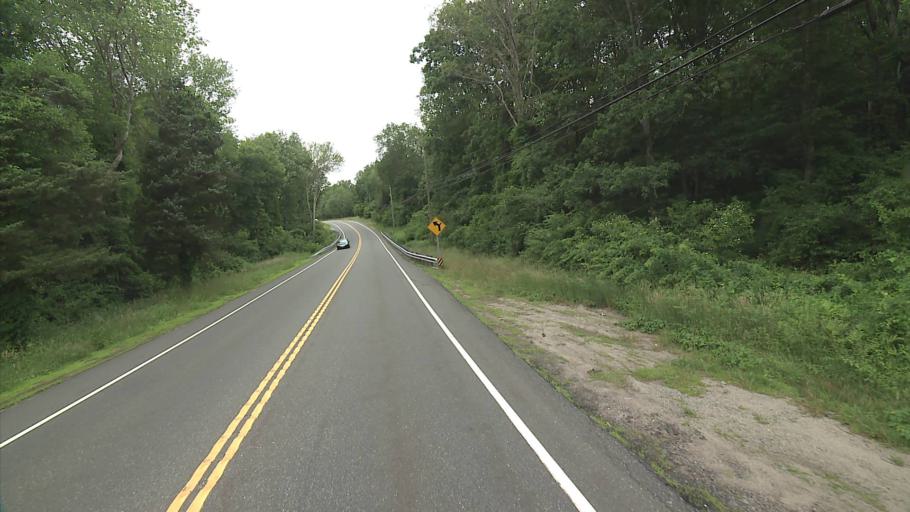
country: US
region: Connecticut
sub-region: New London County
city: Ledyard Center
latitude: 41.4814
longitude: -72.0324
